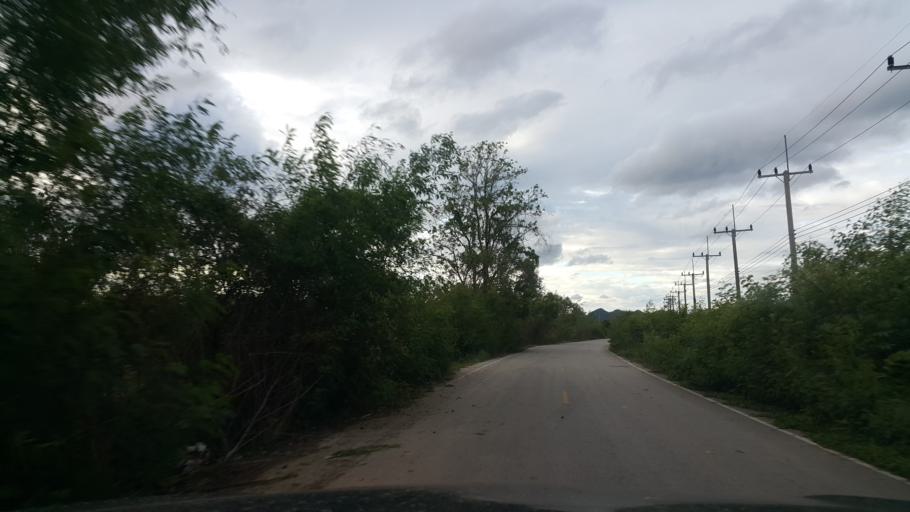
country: TH
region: Sukhothai
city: Thung Saliam
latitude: 17.1657
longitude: 99.5238
